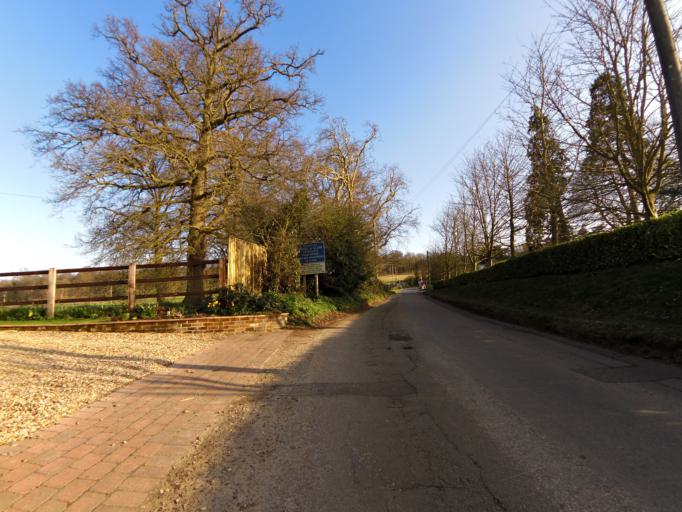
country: GB
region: England
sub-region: Suffolk
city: Kesgrave
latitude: 52.0812
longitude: 1.2540
